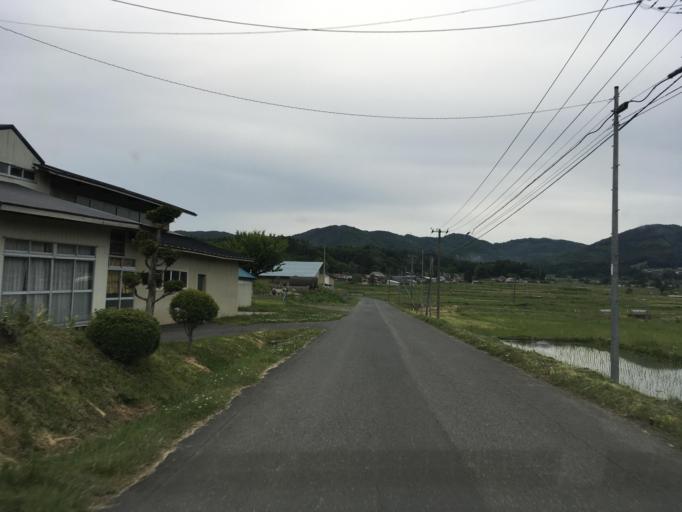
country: JP
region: Iwate
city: Mizusawa
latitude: 39.1613
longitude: 141.3081
